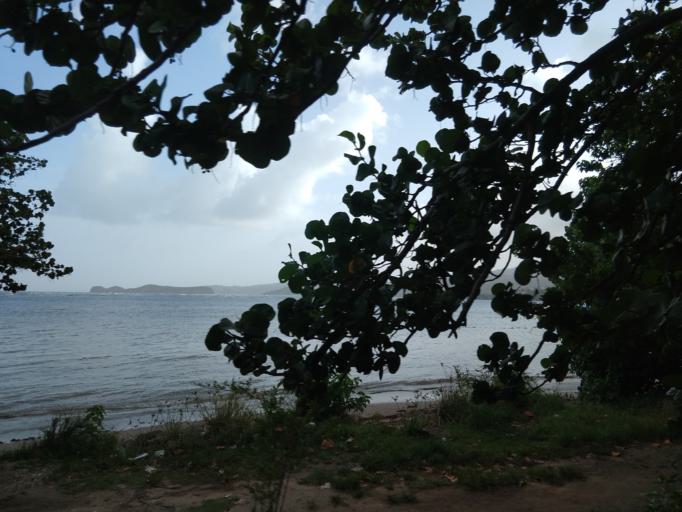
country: GD
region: Saint Andrew
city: Grenville
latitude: 12.1247
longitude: -61.6176
